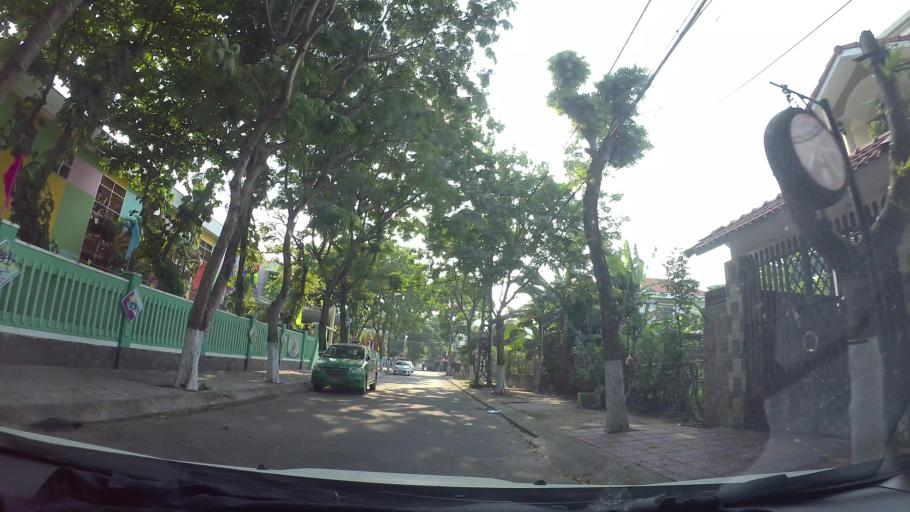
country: VN
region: Da Nang
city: Cam Le
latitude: 16.0228
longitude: 108.2069
